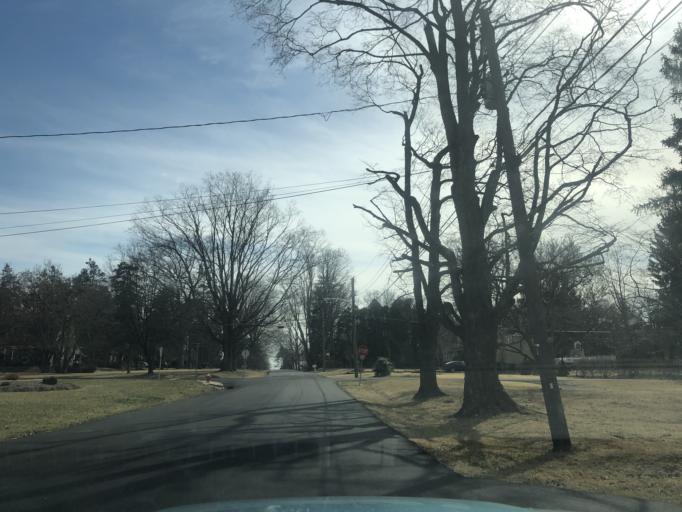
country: US
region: Pennsylvania
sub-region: Bucks County
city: Langhorne Manor
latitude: 40.1671
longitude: -74.9200
